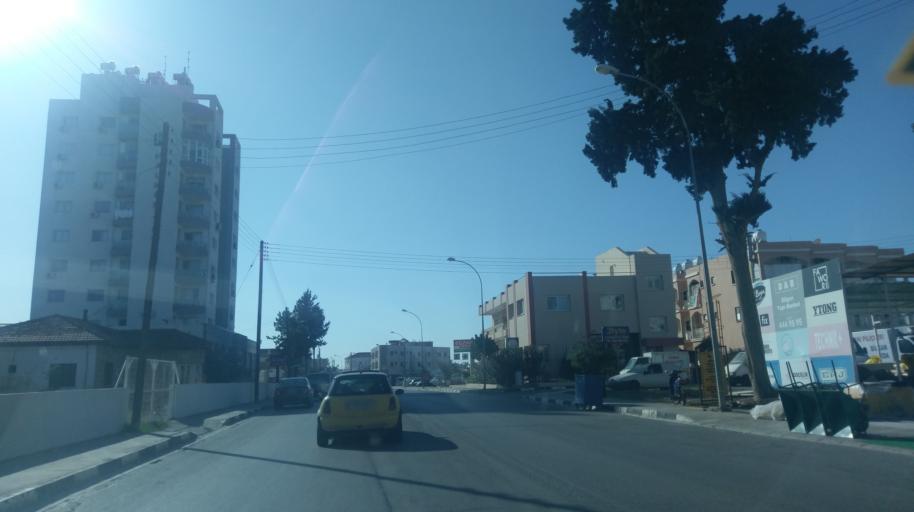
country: CY
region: Ammochostos
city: Famagusta
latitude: 35.1175
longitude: 33.9333
